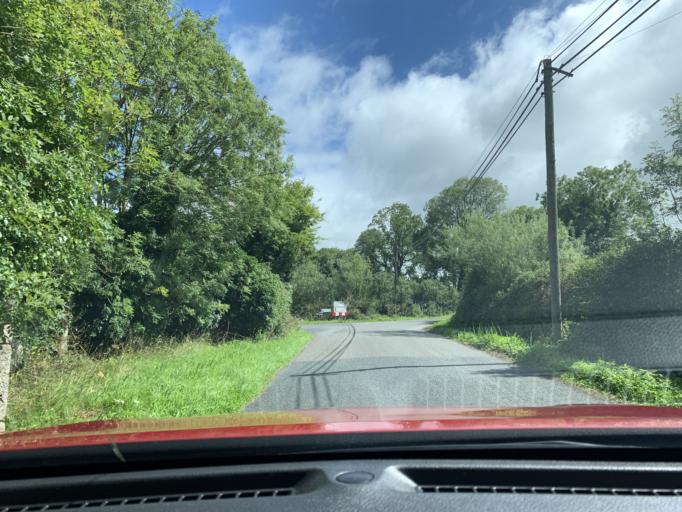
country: IE
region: Connaught
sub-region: County Leitrim
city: Carrick-on-Shannon
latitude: 53.8532
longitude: -8.1608
